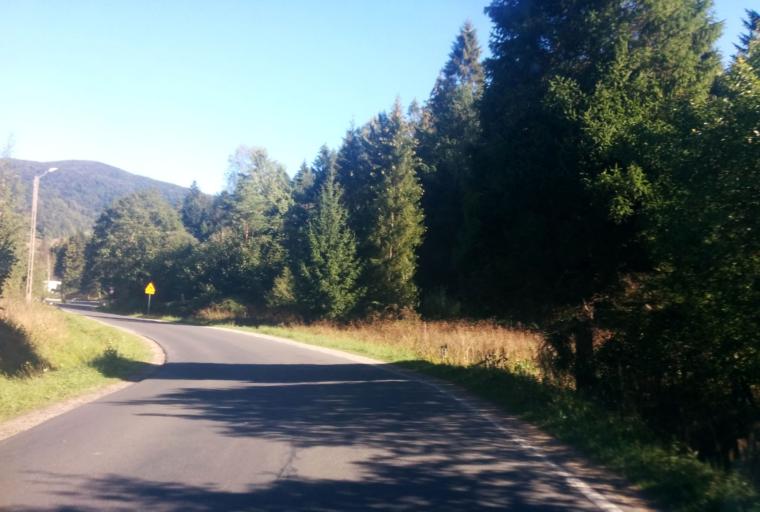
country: PL
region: Subcarpathian Voivodeship
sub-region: Powiat leski
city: Cisna
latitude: 49.2151
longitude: 22.3348
